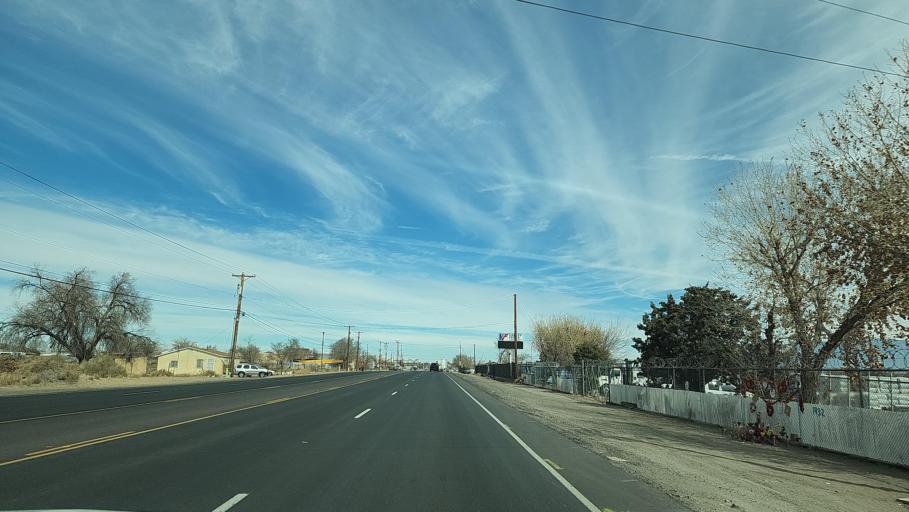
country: US
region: New Mexico
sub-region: Bernalillo County
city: South Valley
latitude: 35.0479
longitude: -106.7085
